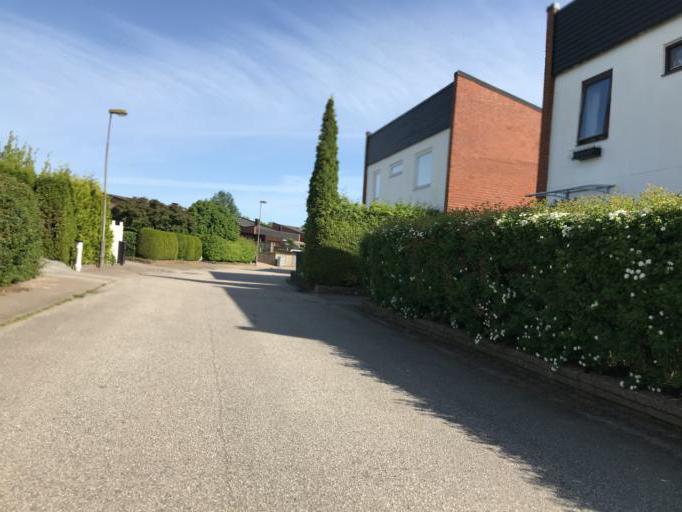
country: SE
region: Skane
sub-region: Malmo
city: Oxie
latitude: 55.5438
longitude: 13.1033
